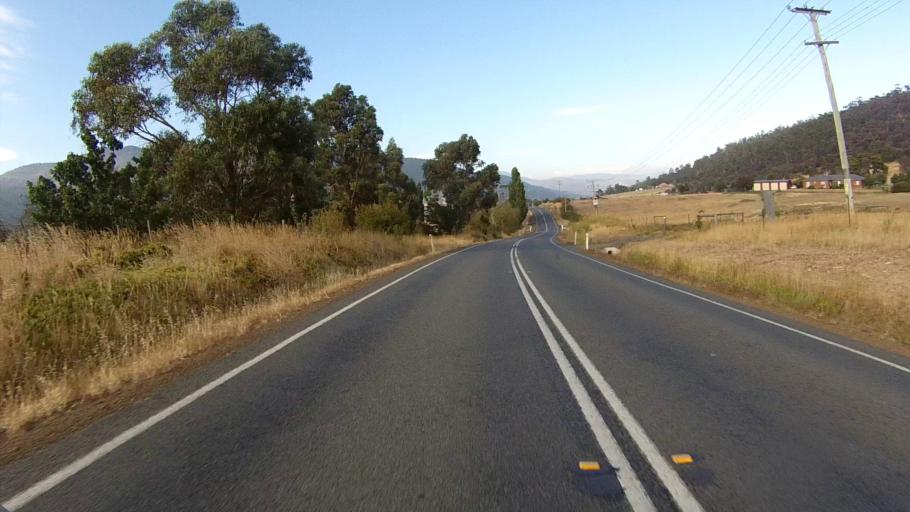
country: AU
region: Tasmania
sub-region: Brighton
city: Bridgewater
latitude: -42.7342
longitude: 147.1757
